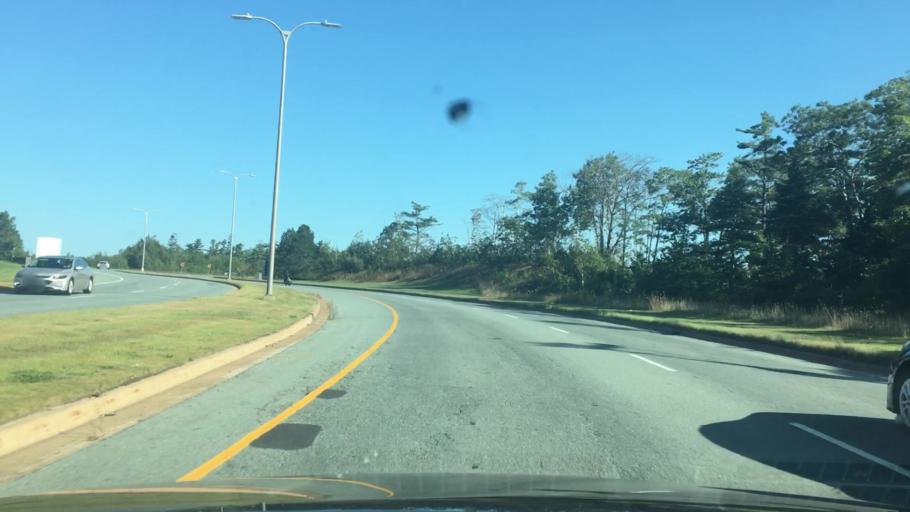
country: CA
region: Nova Scotia
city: Dartmouth
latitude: 44.7193
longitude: -63.5804
